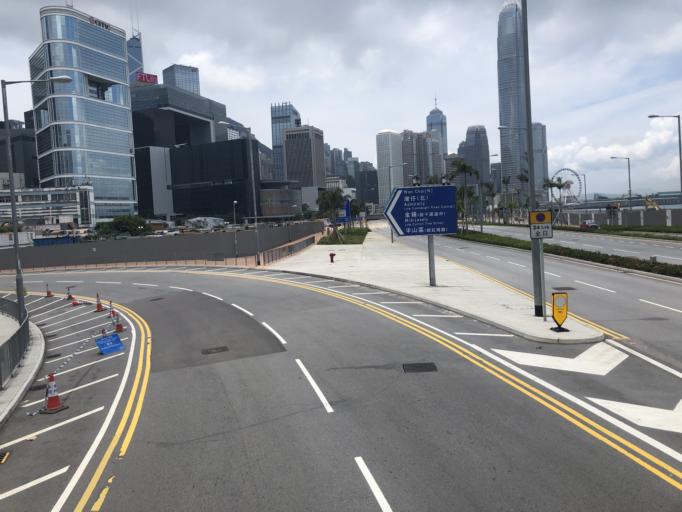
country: HK
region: Wanchai
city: Wan Chai
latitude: 22.2820
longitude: 114.1705
